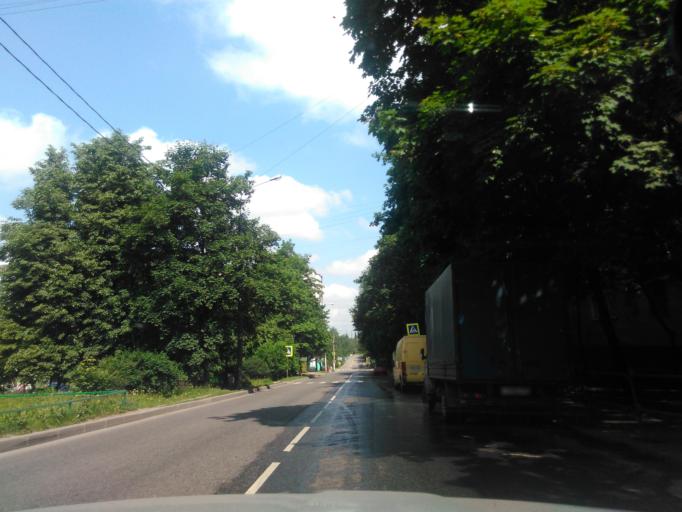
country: RU
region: Moscow
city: Vagonoremont
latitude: 55.8921
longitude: 37.5366
